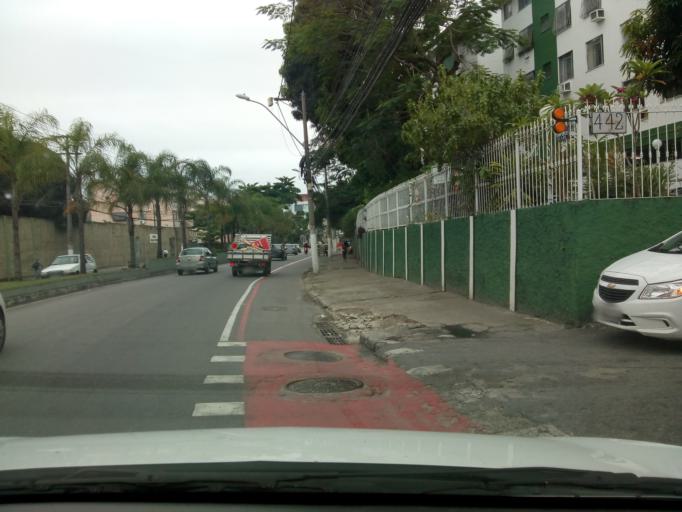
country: BR
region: Rio de Janeiro
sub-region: Niteroi
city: Niteroi
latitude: -22.8743
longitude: -43.1066
